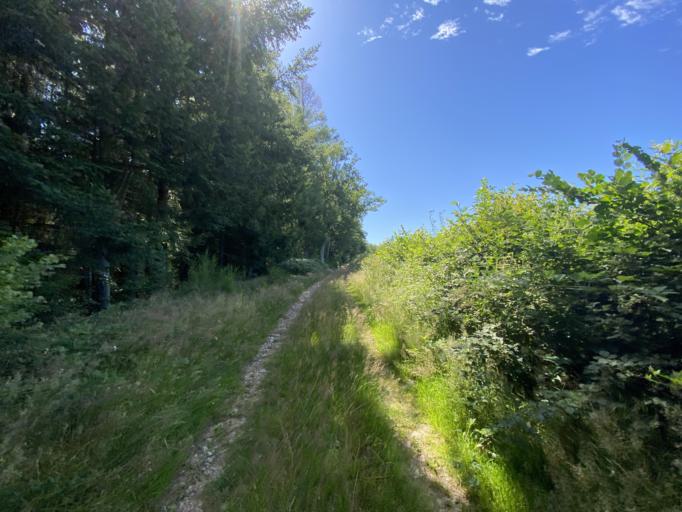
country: FR
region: Bourgogne
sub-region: Departement de la Cote-d'Or
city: Saulieu
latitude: 47.2919
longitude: 4.1270
